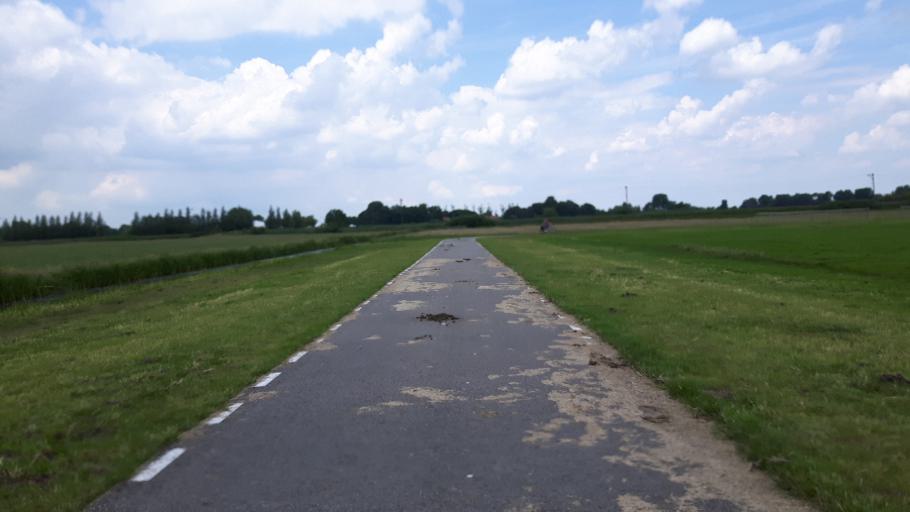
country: NL
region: South Holland
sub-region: Bodegraven-Reeuwijk
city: Bodegraven
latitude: 52.0738
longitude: 4.7840
